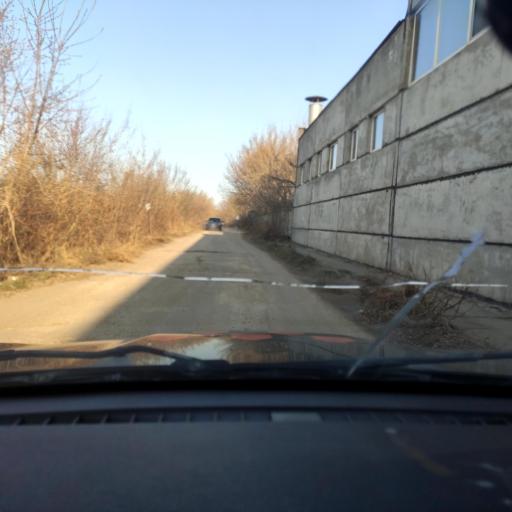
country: RU
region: Samara
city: Tol'yatti
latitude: 53.5840
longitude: 49.2725
